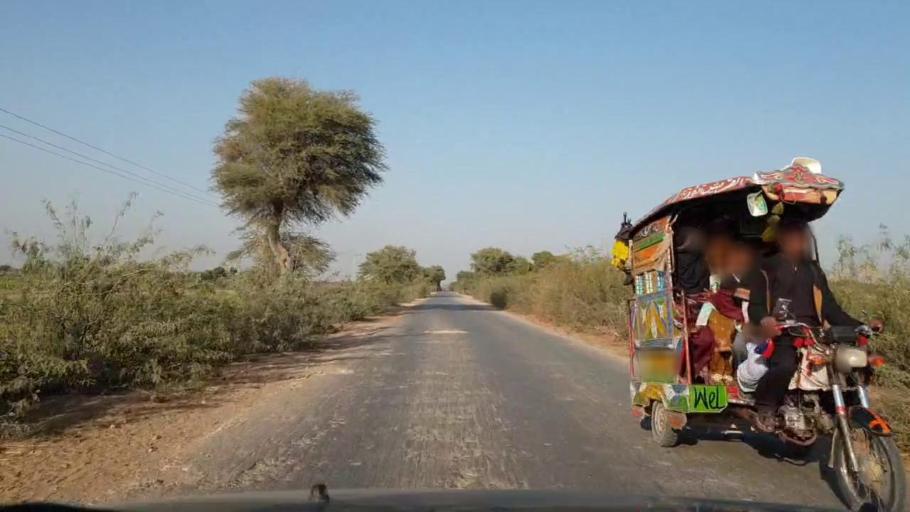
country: PK
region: Sindh
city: Chambar
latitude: 25.2684
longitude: 68.8018
